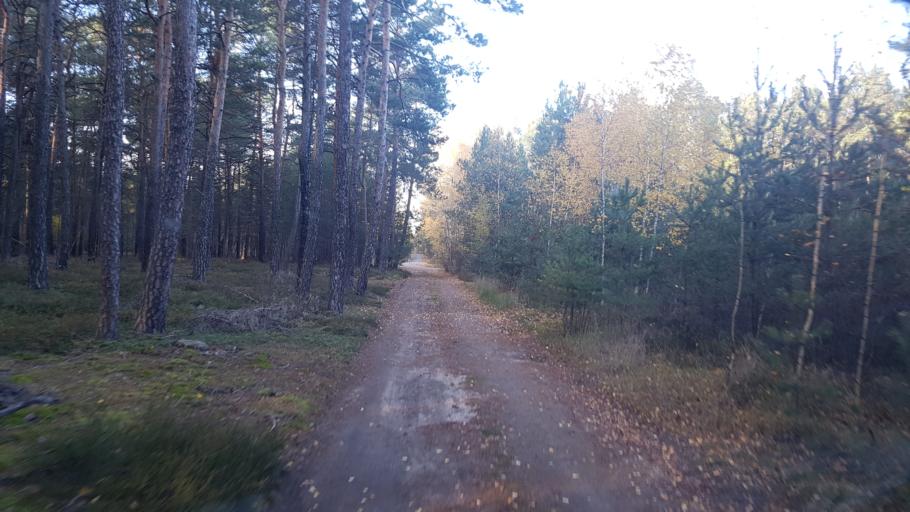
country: DE
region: Brandenburg
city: Calau
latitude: 51.7035
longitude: 13.9530
